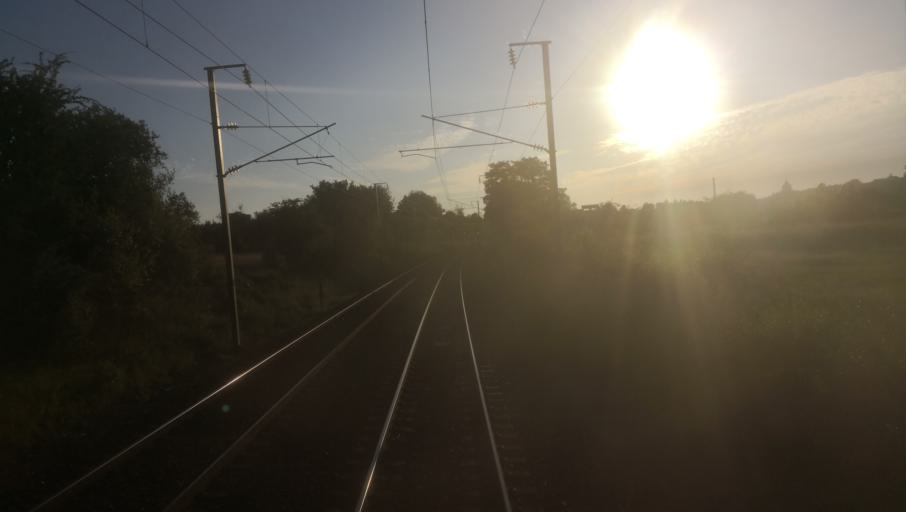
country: FR
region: Lower Normandy
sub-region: Departement du Calvados
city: Beuvillers
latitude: 49.1260
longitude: 0.2678
